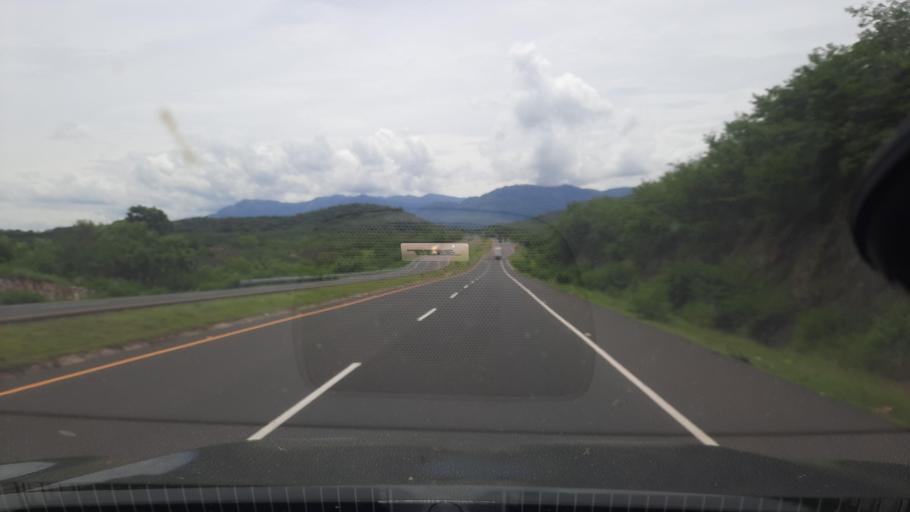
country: HN
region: Valle
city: Aramecina
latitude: 13.6838
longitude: -87.7267
